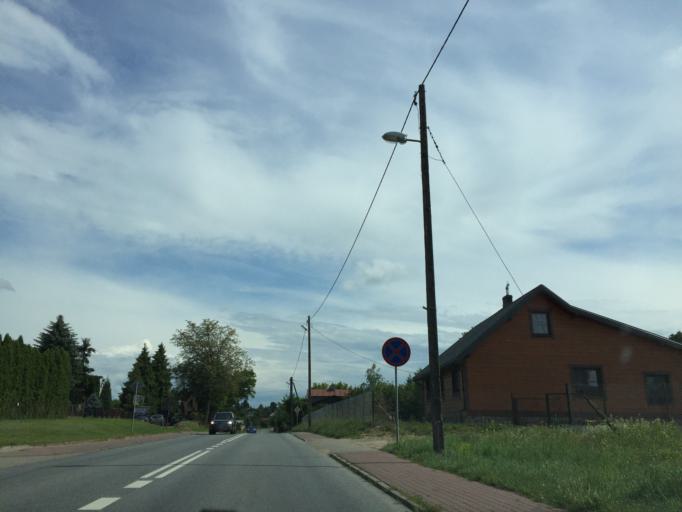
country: PL
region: Masovian Voivodeship
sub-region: Powiat losicki
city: Sarnaki
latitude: 52.3185
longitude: 22.8852
